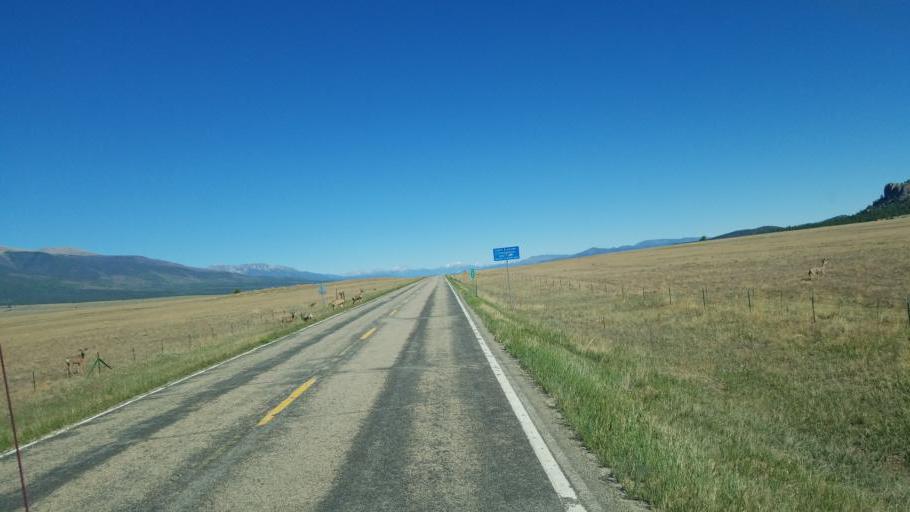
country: US
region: Colorado
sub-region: Custer County
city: Westcliffe
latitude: 38.2013
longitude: -105.5348
